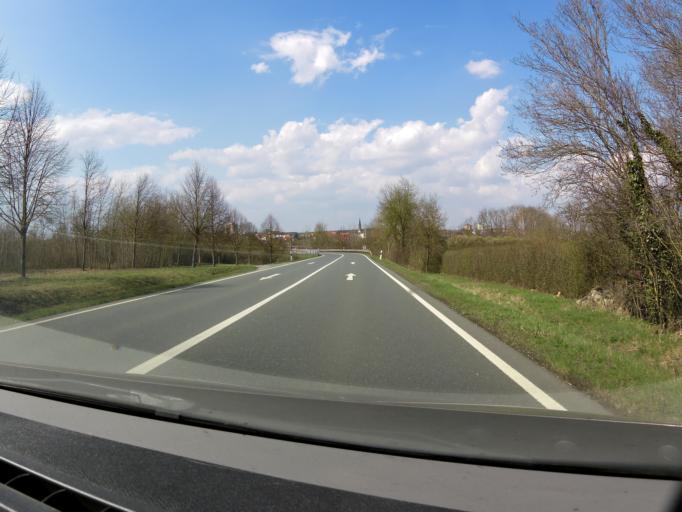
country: DE
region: Bavaria
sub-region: Regierungsbezirk Unterfranken
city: Rottendorf
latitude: 49.7853
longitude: 10.0337
